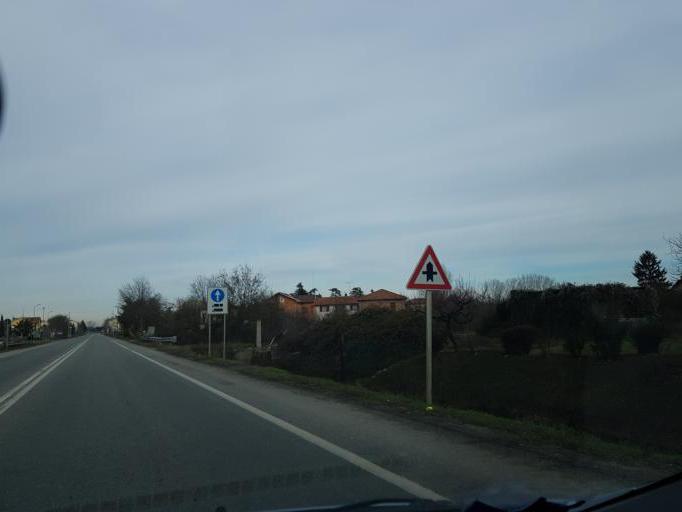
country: IT
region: Piedmont
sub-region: Provincia di Alessandria
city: Novi Ligure
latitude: 44.7606
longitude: 8.8069
